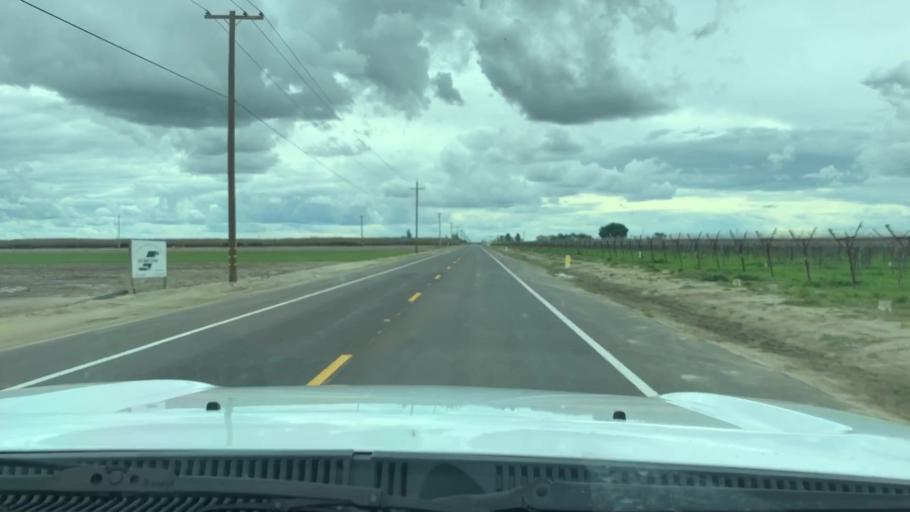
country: US
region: California
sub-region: Fresno County
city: Laton
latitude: 36.5093
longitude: -119.6830
